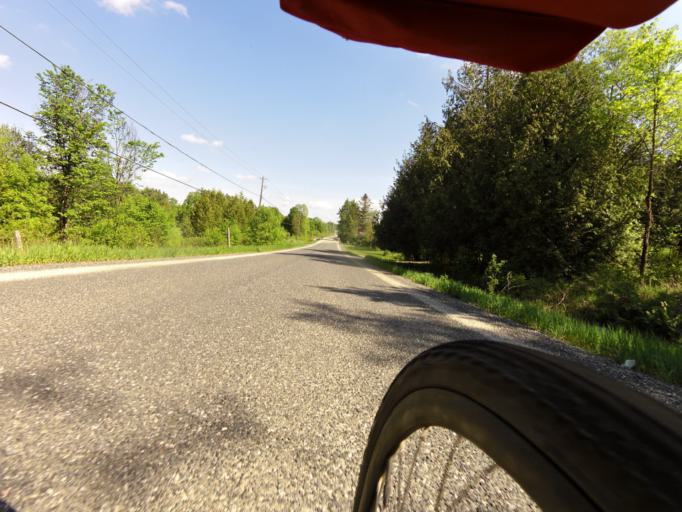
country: CA
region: Ontario
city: Perth
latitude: 45.1232
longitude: -76.5223
